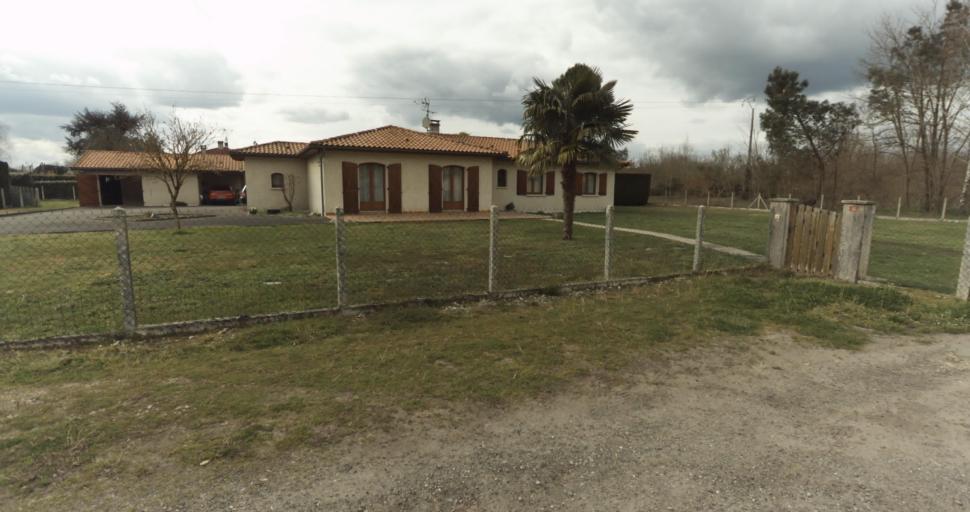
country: FR
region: Aquitaine
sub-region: Departement des Landes
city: Roquefort
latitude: 44.0413
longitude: -0.3266
